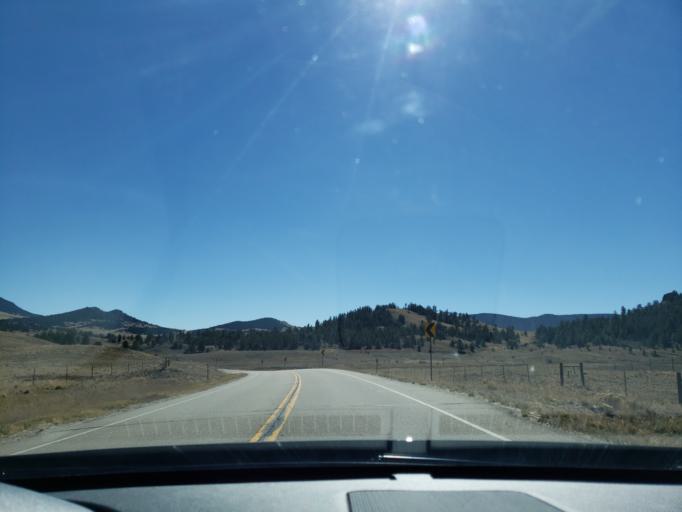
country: US
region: Colorado
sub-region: Chaffee County
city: Buena Vista
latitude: 38.8646
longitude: -105.6642
